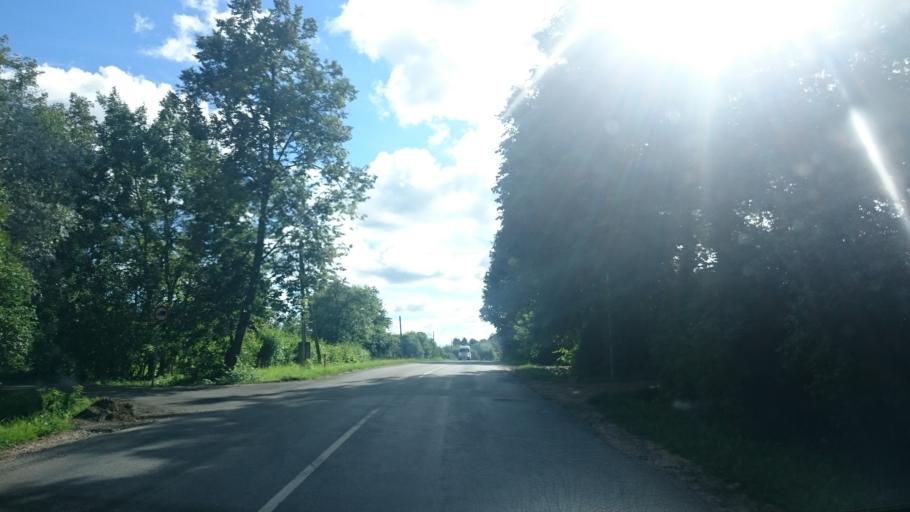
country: LV
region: Aizpute
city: Aizpute
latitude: 56.7206
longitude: 21.5930
